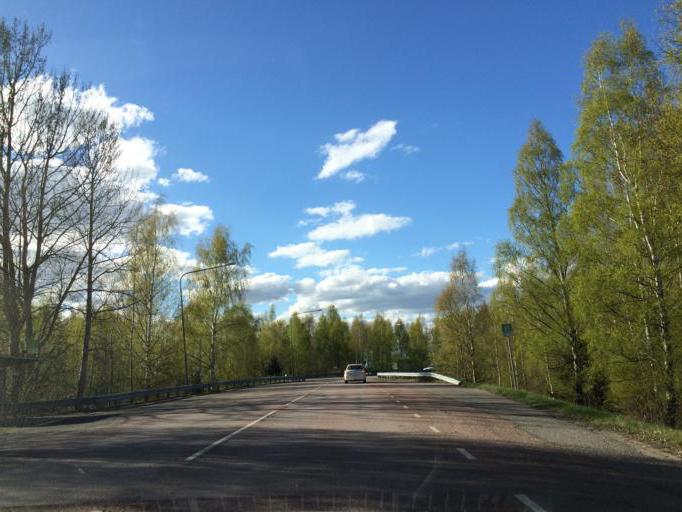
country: SE
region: Soedermanland
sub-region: Eskilstuna Kommun
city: Kvicksund
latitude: 59.4444
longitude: 16.3331
